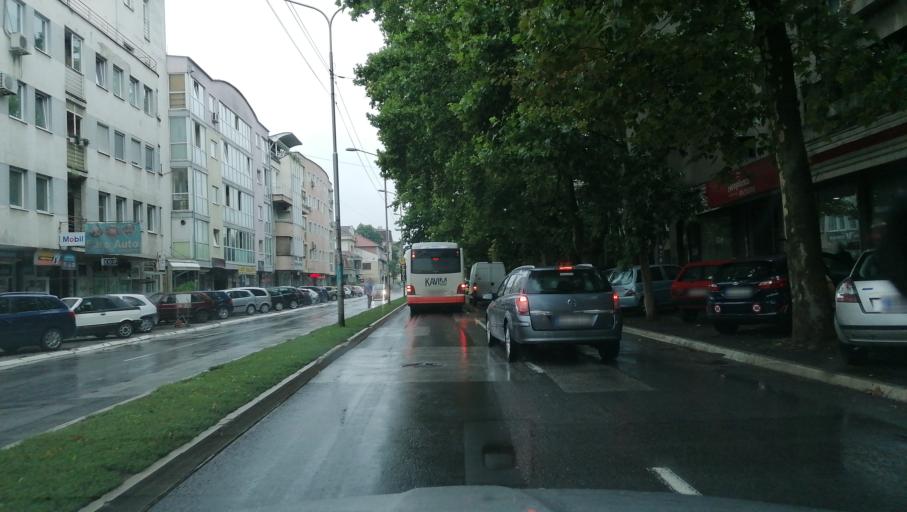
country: RS
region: Central Serbia
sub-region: Raski Okrug
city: Kraljevo
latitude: 43.7261
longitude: 20.6945
